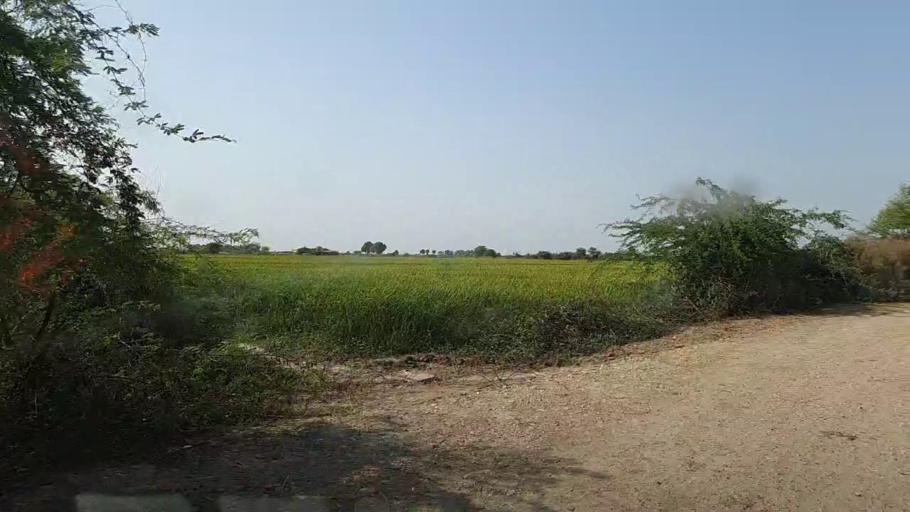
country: PK
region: Sindh
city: Kario
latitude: 24.7494
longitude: 68.4638
